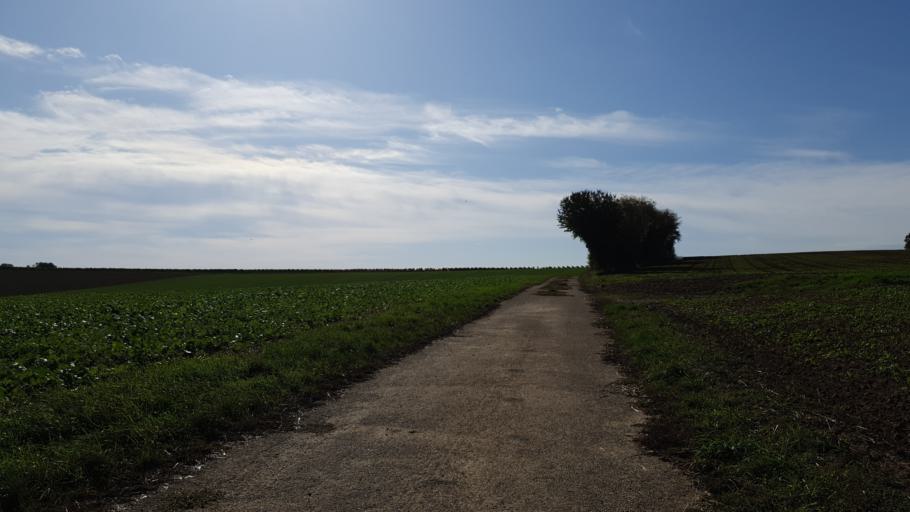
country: DE
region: Rheinland-Pfalz
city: Niederhorbach
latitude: 49.1133
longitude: 8.0468
